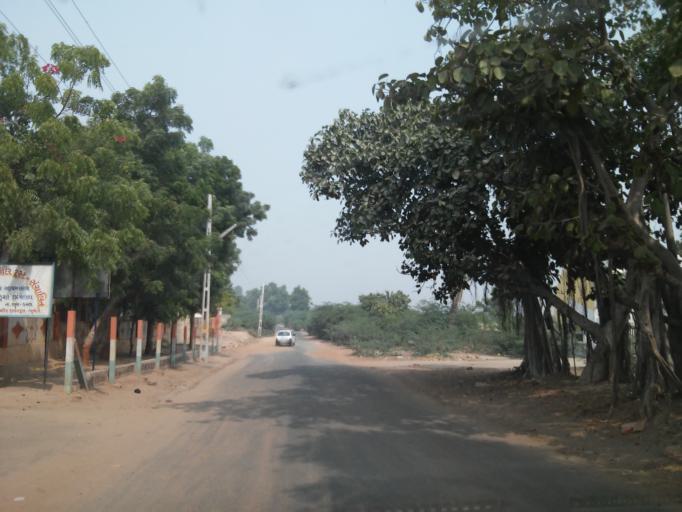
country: IN
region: Gujarat
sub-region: Kachchh
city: Bhuj
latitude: 23.2293
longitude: 69.7370
